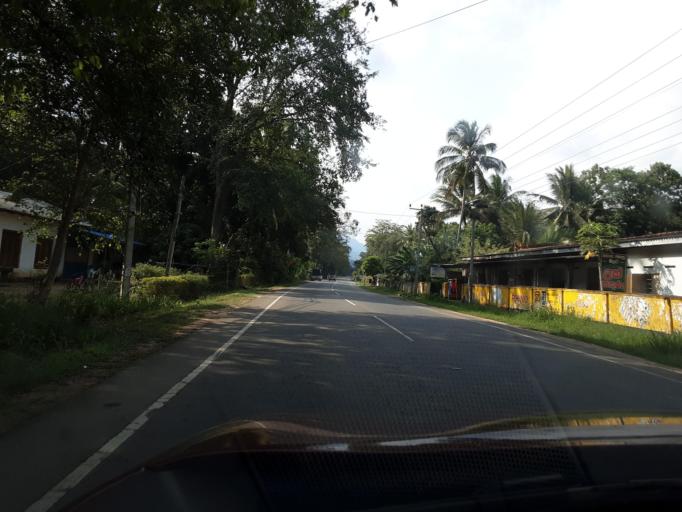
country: LK
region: Uva
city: Haputale
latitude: 6.6786
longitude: 81.1109
